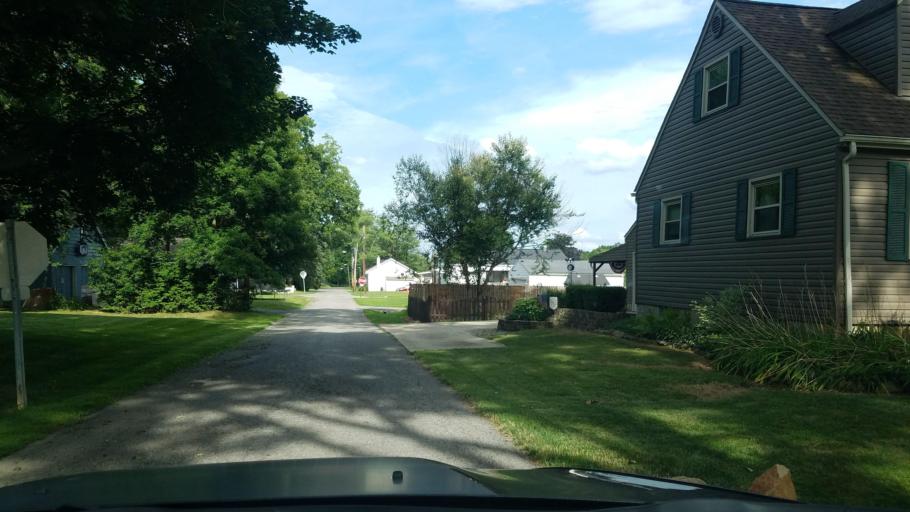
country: US
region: Ohio
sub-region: Trumbull County
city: Niles
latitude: 41.1729
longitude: -80.7783
